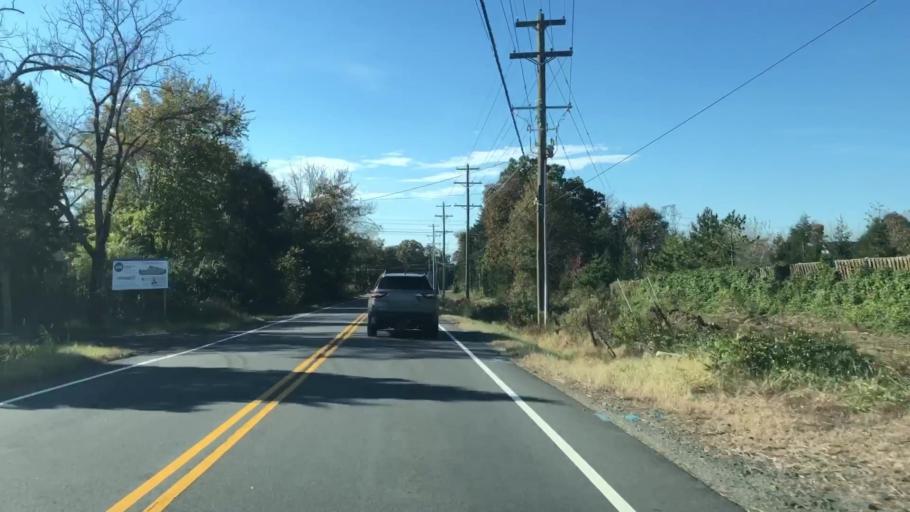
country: US
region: Virginia
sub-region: Prince William County
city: Linton Hall
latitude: 38.7338
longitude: -77.5867
